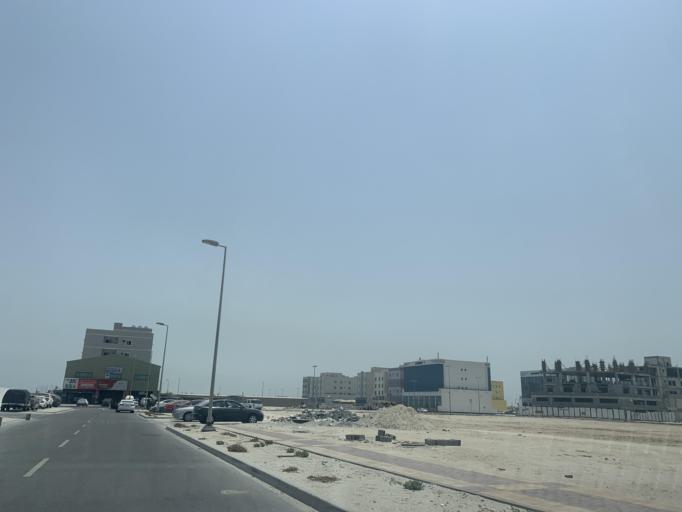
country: BH
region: Muharraq
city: Al Hadd
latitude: 26.2575
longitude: 50.6670
